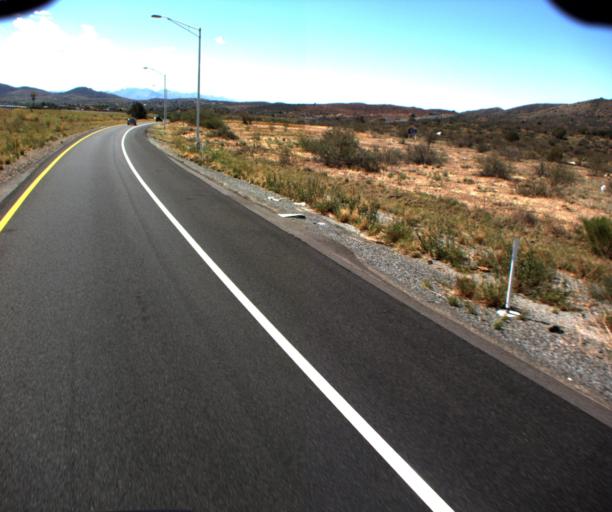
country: US
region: Arizona
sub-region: Yavapai County
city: Cordes Lakes
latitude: 34.3303
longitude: -112.1234
